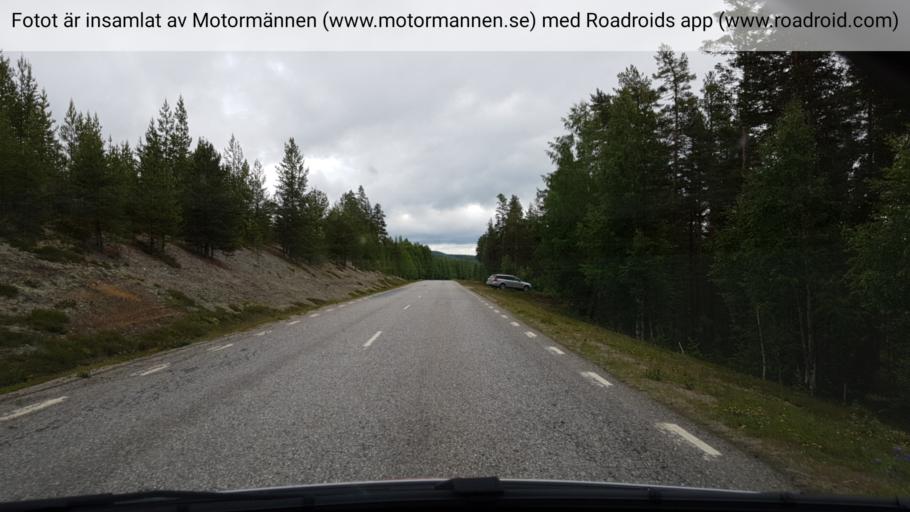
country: SE
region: Vaesterbotten
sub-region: Norsjo Kommun
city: Norsjoe
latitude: 64.6746
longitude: 19.2562
